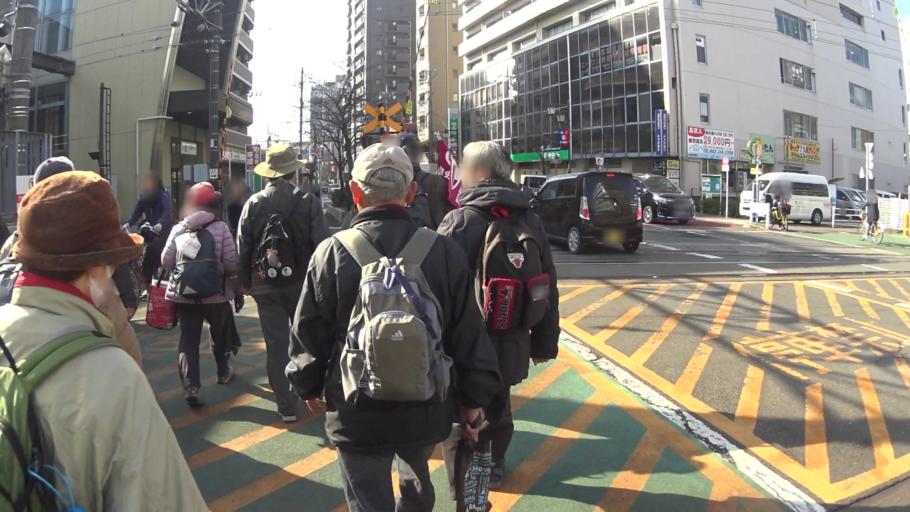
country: JP
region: Tokyo
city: Kokubunji
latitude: 35.6690
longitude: 139.4949
